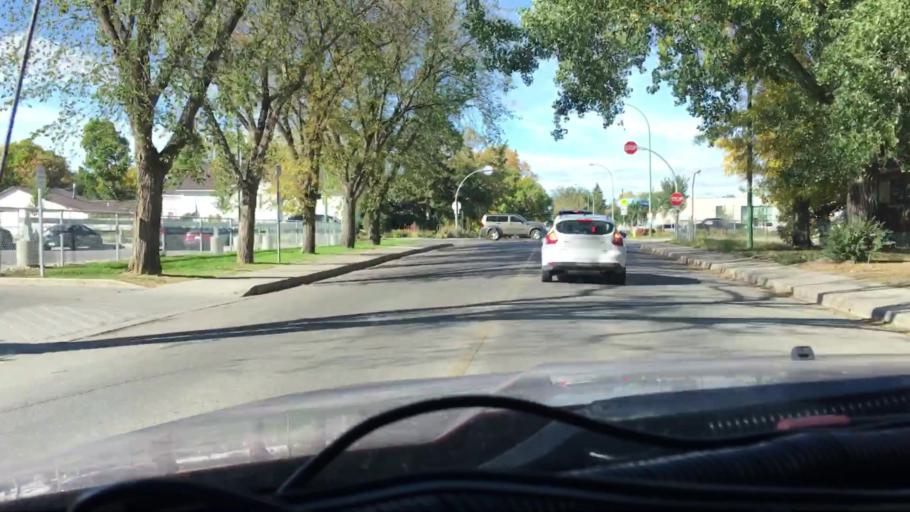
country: CA
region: Saskatchewan
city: Regina
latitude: 50.4578
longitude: -104.6312
